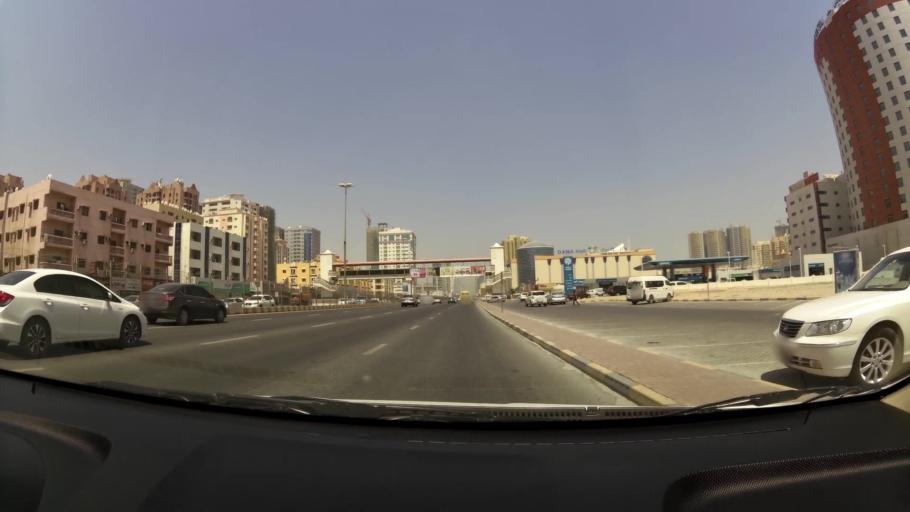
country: AE
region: Ajman
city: Ajman
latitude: 25.3890
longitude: 55.4615
